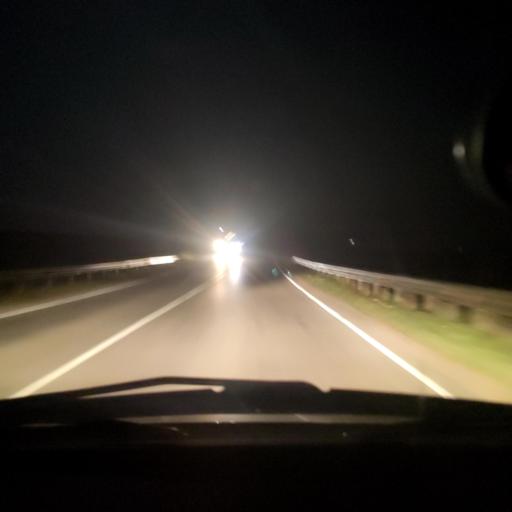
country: RU
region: Bashkortostan
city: Iglino
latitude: 54.9219
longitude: 56.4781
